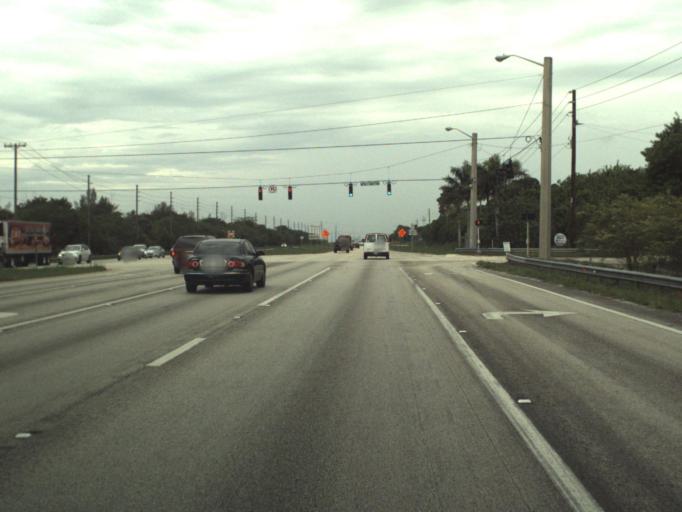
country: US
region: Florida
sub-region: Palm Beach County
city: Loxahatchee Groves
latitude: 26.6832
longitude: -80.2904
